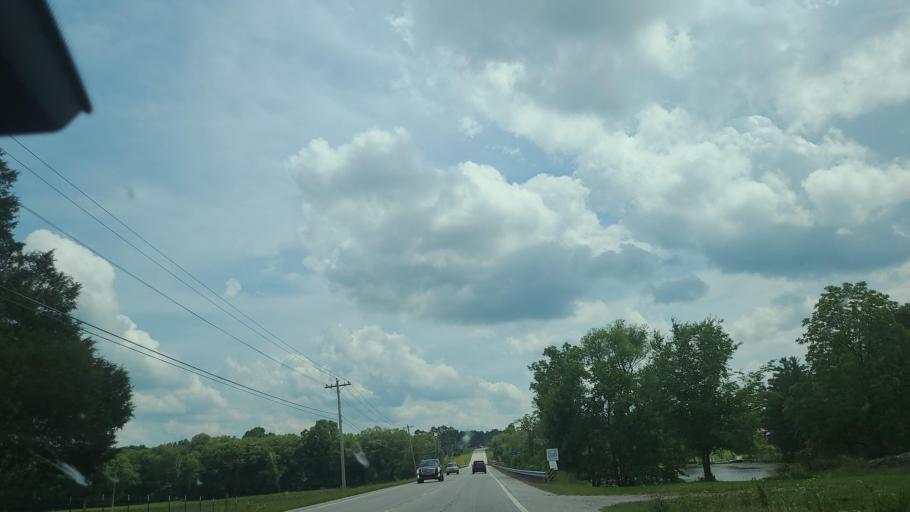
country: US
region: Tennessee
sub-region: Cumberland County
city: Lake Tansi
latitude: 35.8097
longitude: -85.0206
